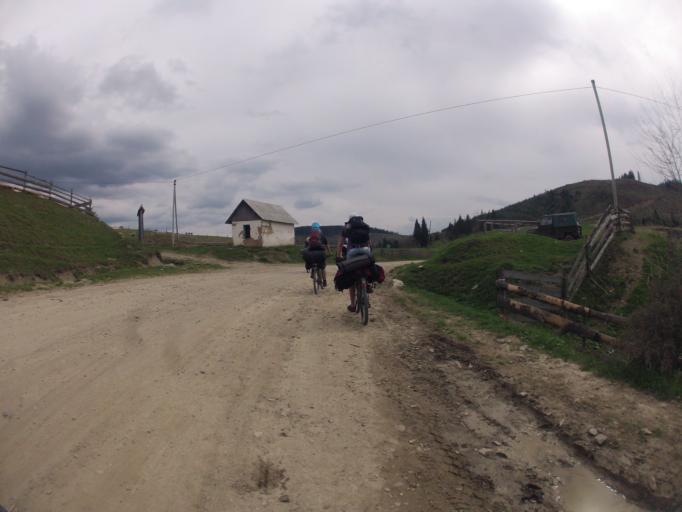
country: UA
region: Chernivtsi
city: Putyla
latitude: 47.8898
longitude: 25.1659
